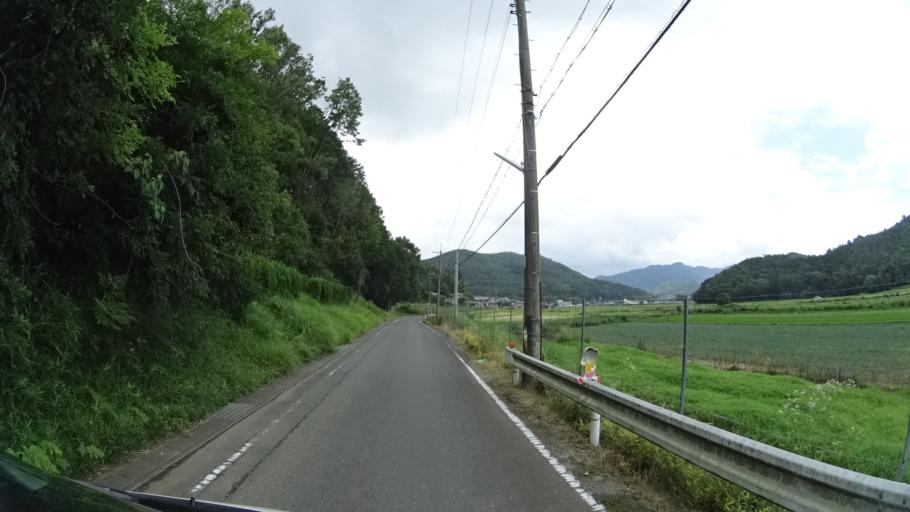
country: JP
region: Kyoto
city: Kameoka
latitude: 35.0879
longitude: 135.4926
